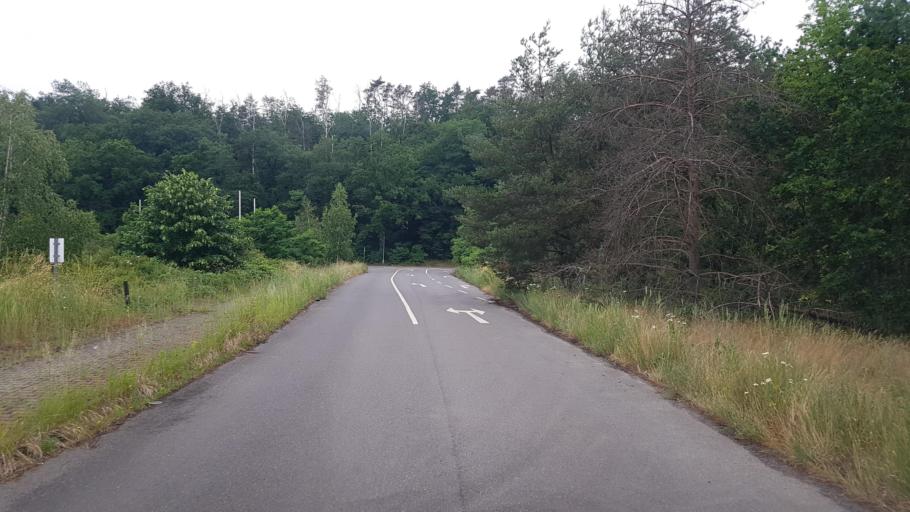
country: DE
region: Brandenburg
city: Senftenberg
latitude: 51.4967
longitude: 13.9597
